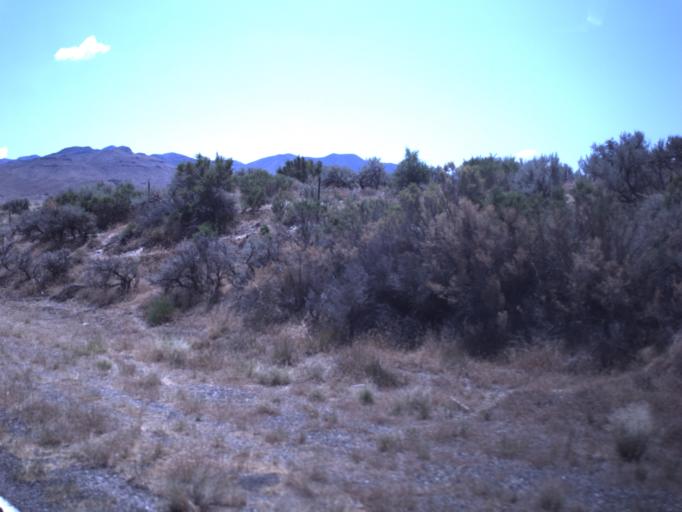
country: US
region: Utah
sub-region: Millard County
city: Delta
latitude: 39.3544
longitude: -112.4099
